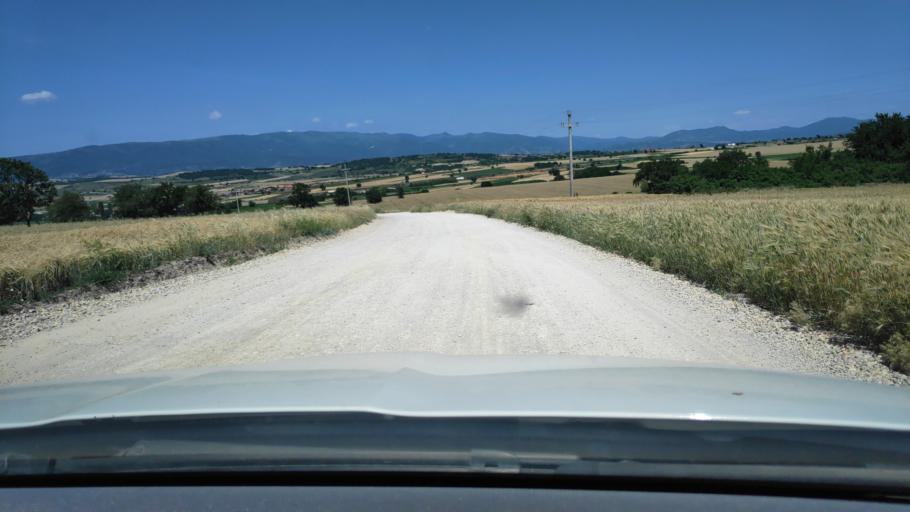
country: MK
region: Kumanovo
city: Romanovce
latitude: 42.0767
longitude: 21.7161
